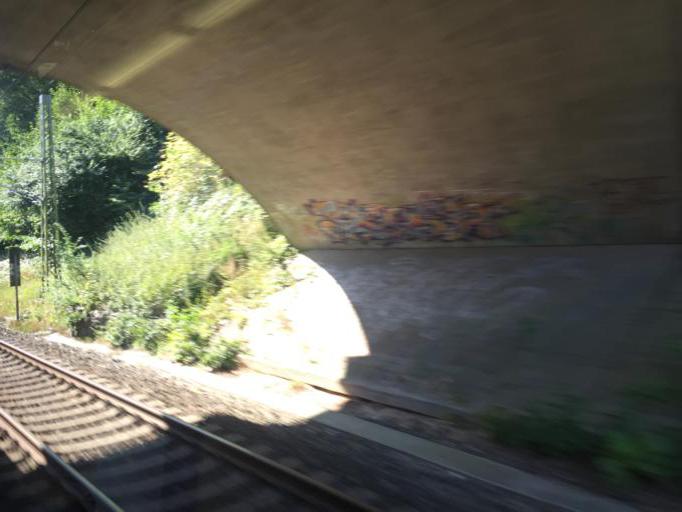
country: DE
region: Schleswig-Holstein
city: Luebeck
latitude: 53.8914
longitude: 10.6897
